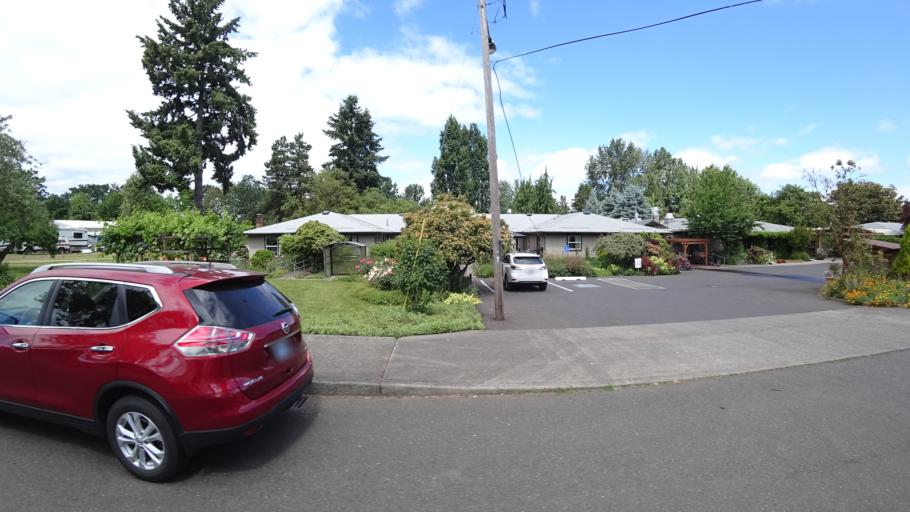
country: US
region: Oregon
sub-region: Washington County
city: West Haven
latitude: 45.6029
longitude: -122.7674
